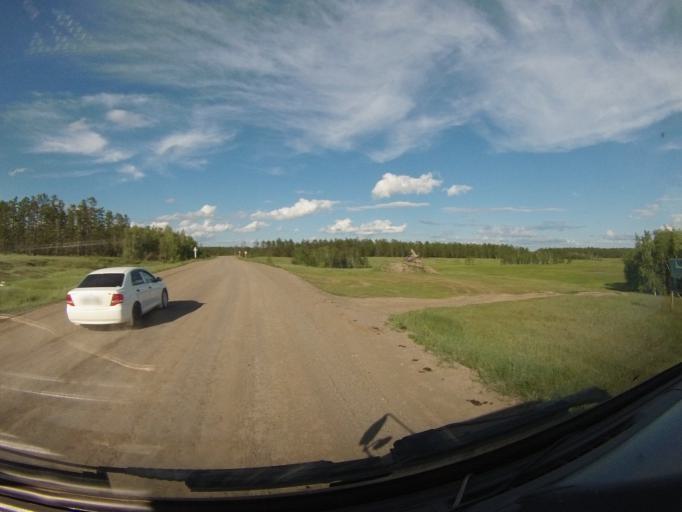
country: RU
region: Sakha
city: Ytyk-Kyuyel'
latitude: 62.2226
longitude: 133.2805
